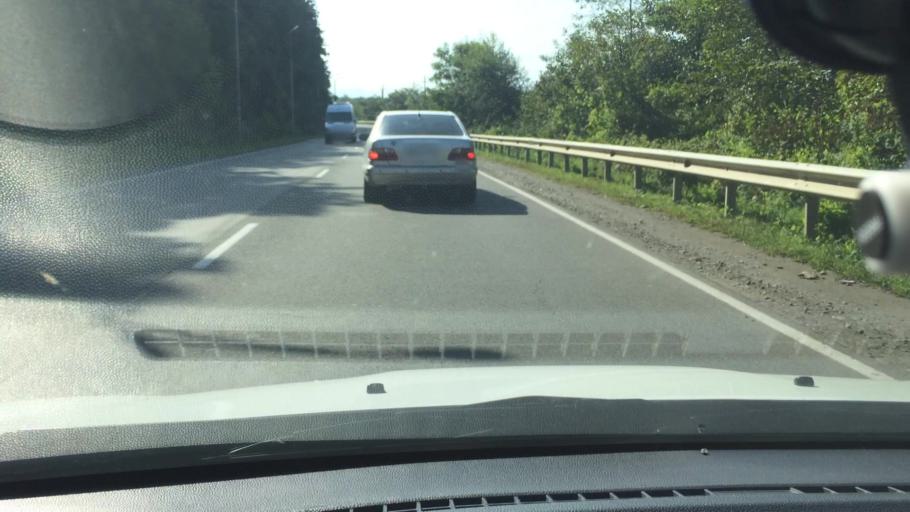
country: GE
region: Guria
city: Urek'i
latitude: 41.9911
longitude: 41.7812
